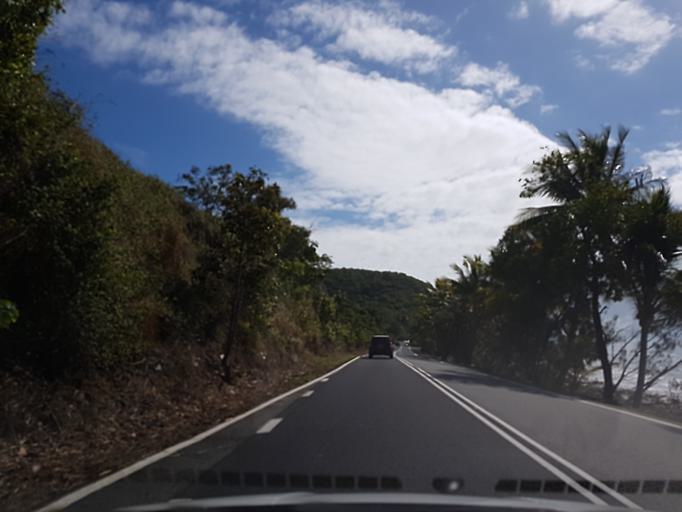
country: AU
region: Queensland
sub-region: Cairns
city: Port Douglas
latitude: -16.5815
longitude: 145.5124
